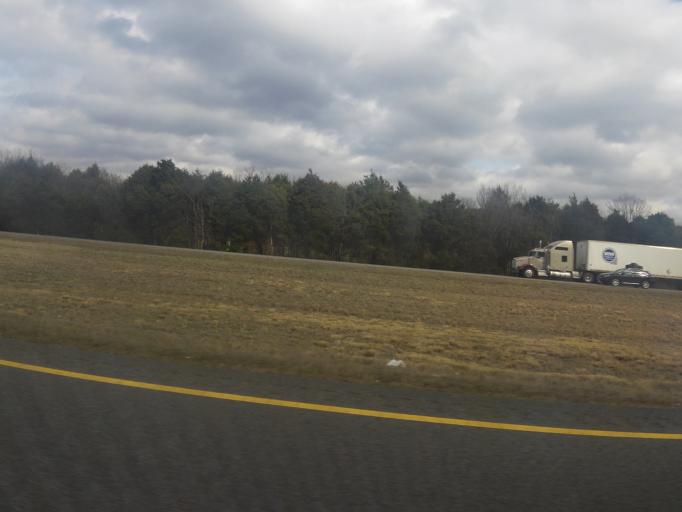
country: US
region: Tennessee
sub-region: Rutherford County
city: Plainview
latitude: 35.6725
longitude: -86.2822
